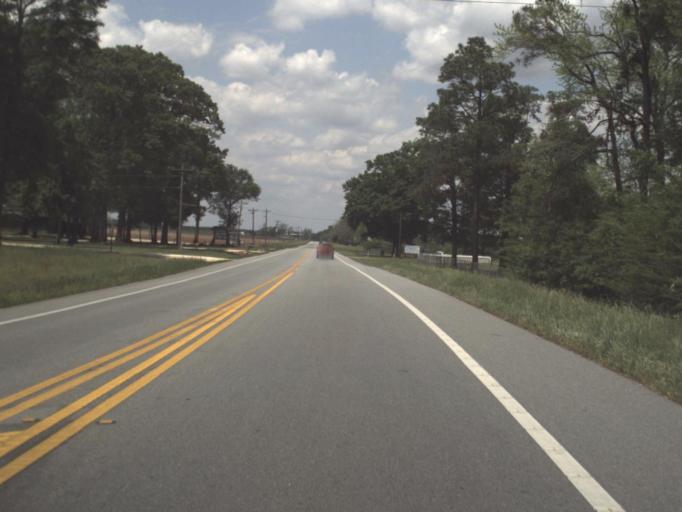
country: US
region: Alabama
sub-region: Escambia County
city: Atmore
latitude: 30.9653
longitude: -87.4852
